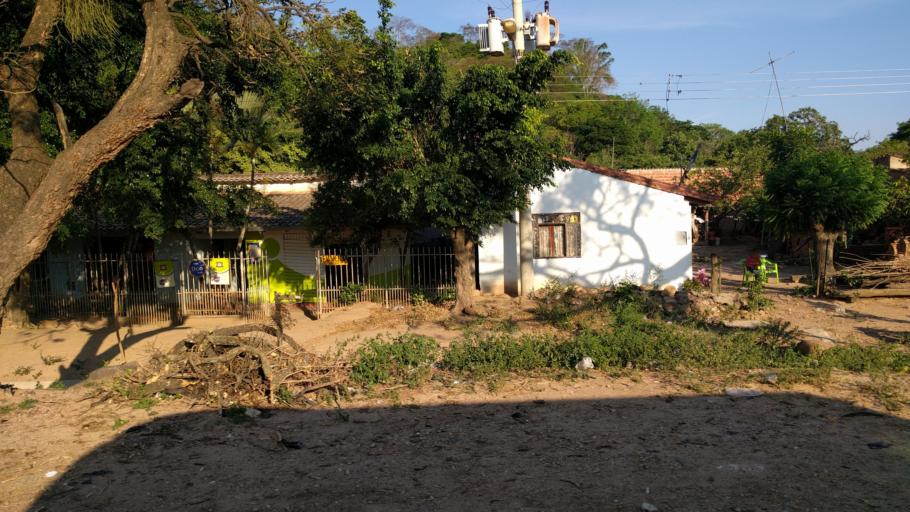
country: BO
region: Santa Cruz
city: Limoncito
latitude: -18.0098
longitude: -63.3924
